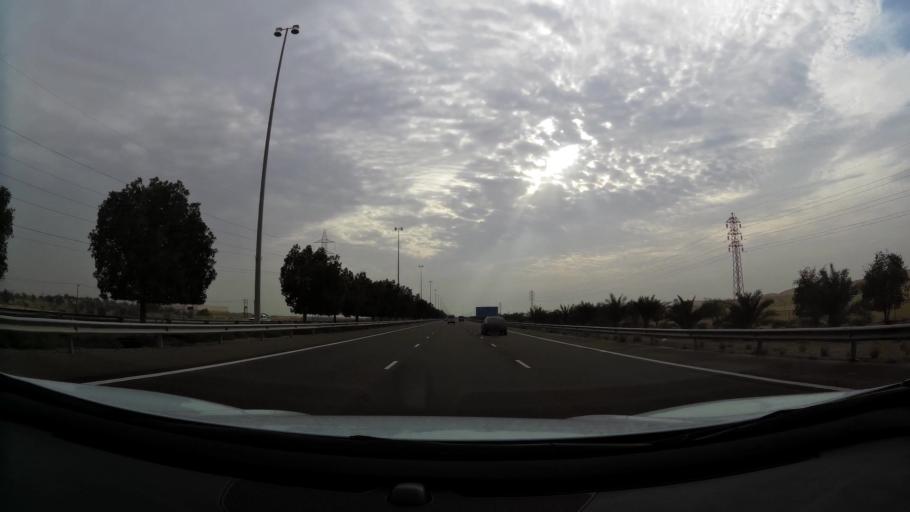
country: AE
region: Abu Dhabi
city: Abu Dhabi
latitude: 24.1951
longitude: 54.9348
